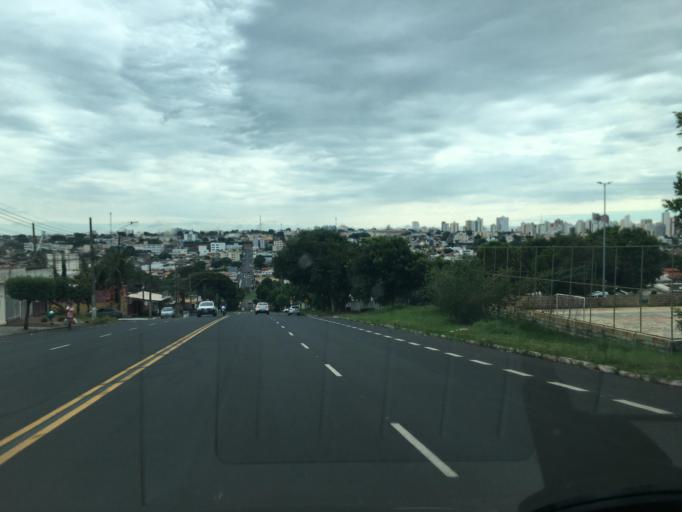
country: BR
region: Minas Gerais
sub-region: Uberlandia
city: Uberlandia
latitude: -18.9228
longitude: -48.3055
